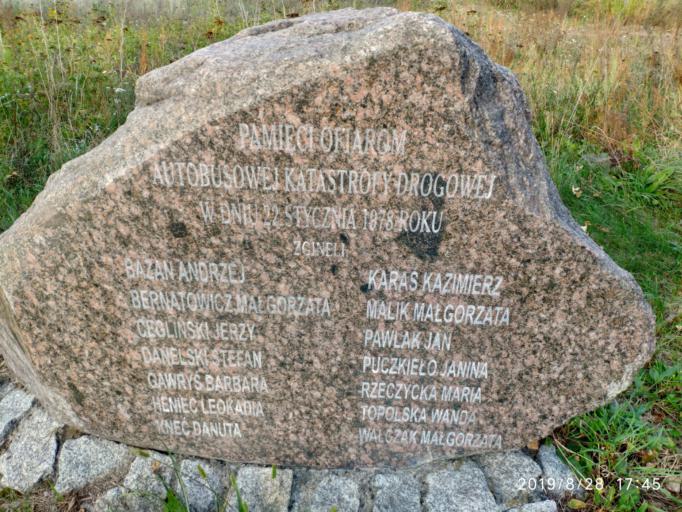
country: PL
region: Lubusz
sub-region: Powiat krosnienski
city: Krosno Odrzanskie
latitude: 52.0712
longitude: 15.0603
